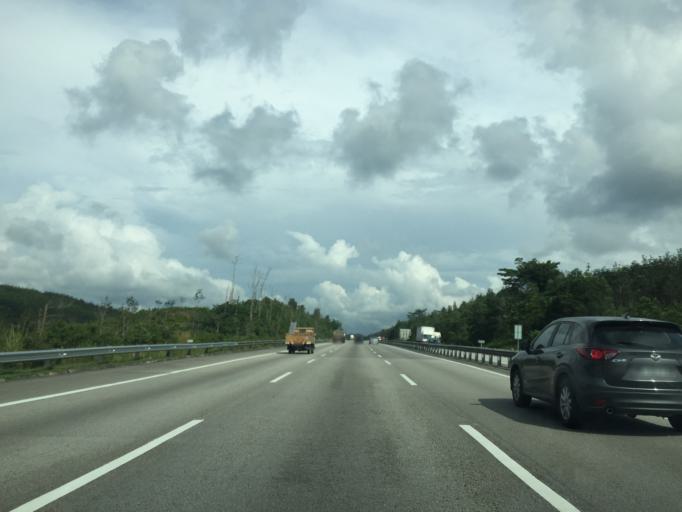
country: MY
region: Selangor
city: Serendah
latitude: 3.5165
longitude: 101.5272
